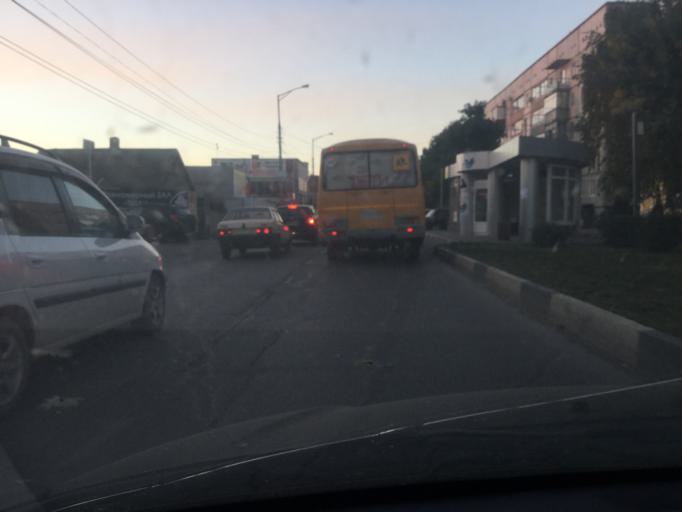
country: RU
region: Krasnodarskiy
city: Slavyansk-na-Kubani
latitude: 45.2545
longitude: 38.1129
